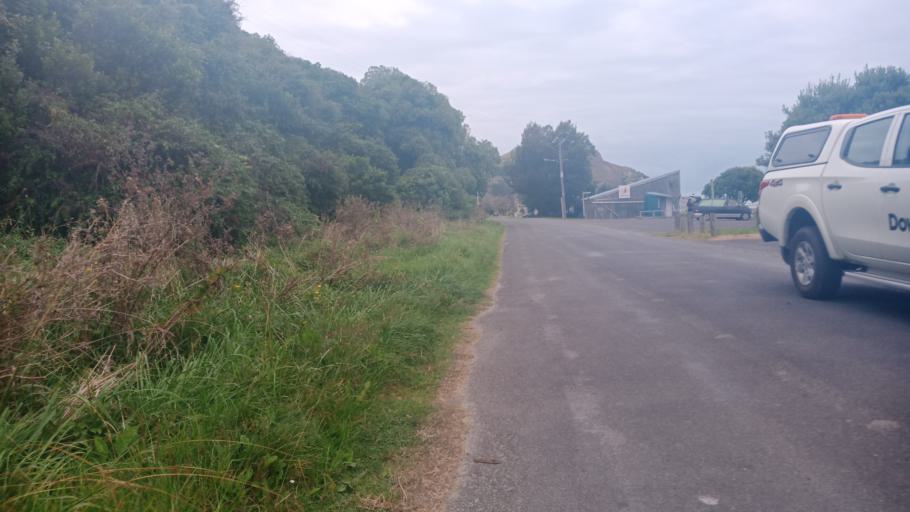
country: NZ
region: Gisborne
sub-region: Gisborne District
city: Gisborne
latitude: -38.6815
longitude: 178.0296
